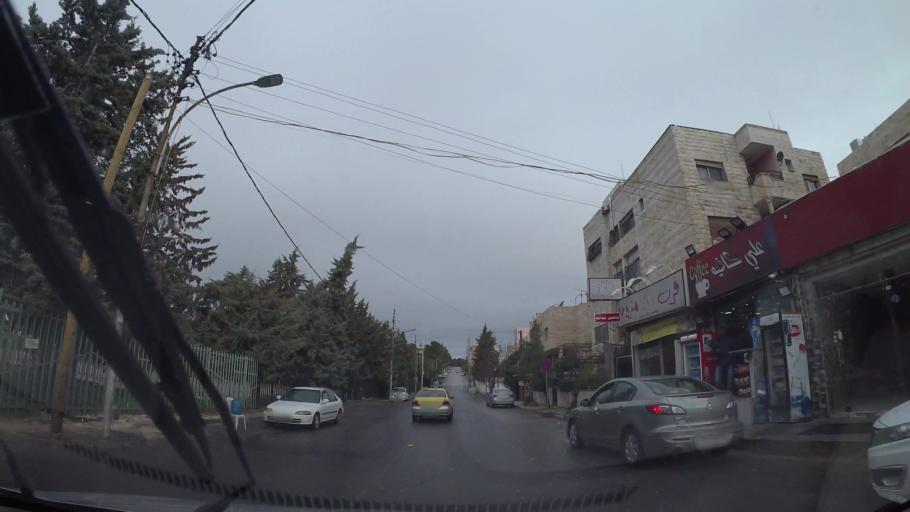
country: JO
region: Amman
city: Al Jubayhah
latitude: 32.0138
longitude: 35.8767
